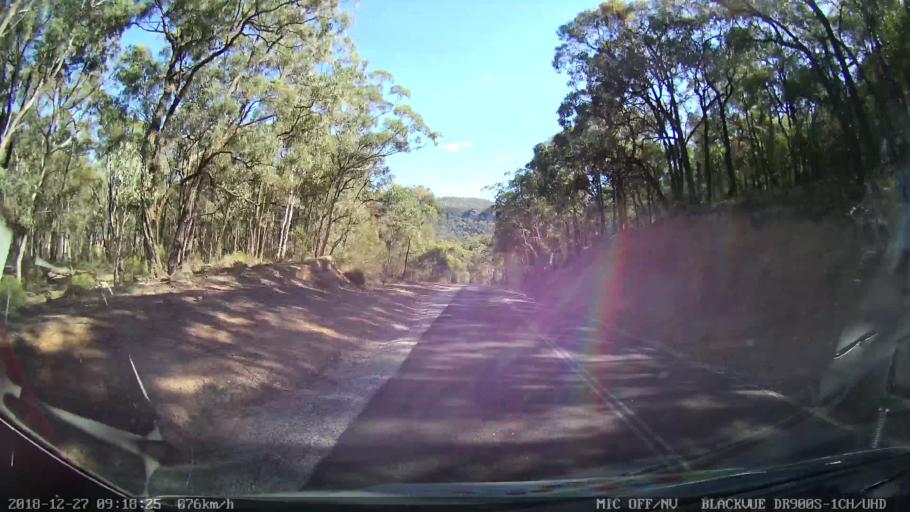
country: AU
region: New South Wales
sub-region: Lithgow
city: Portland
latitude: -33.1272
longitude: 150.0450
